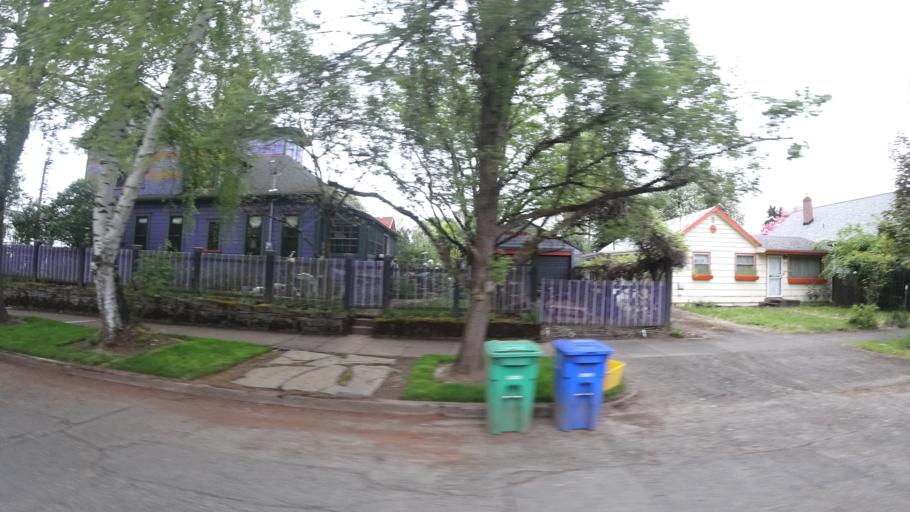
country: US
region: Oregon
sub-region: Clackamas County
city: Milwaukie
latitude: 45.4684
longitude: -122.6570
